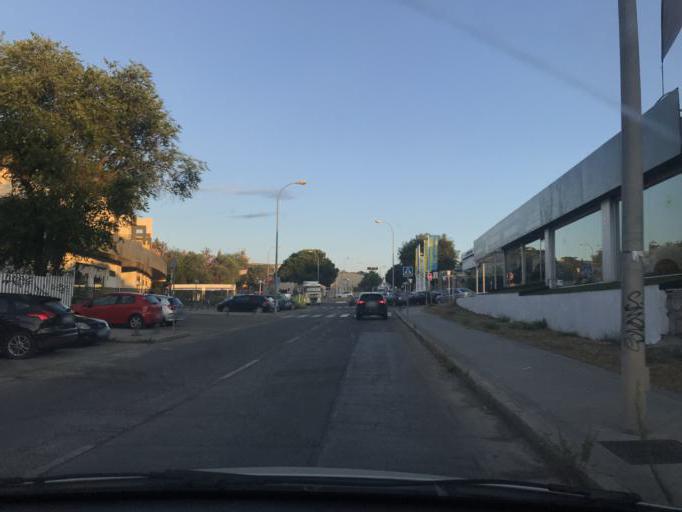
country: ES
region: Madrid
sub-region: Provincia de Madrid
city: Alcobendas
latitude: 40.5351
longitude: -3.6462
